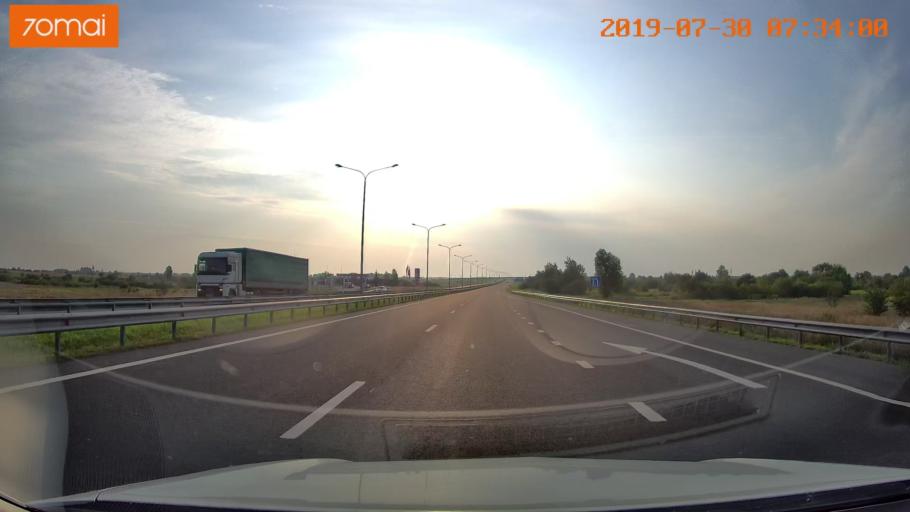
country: RU
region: Kaliningrad
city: Gvardeysk
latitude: 54.6713
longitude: 21.0609
